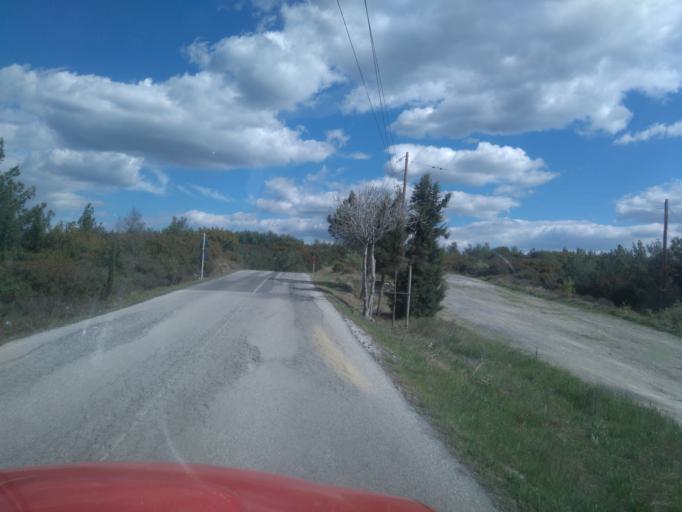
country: GR
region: Central Macedonia
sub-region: Nomos Thessalonikis
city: Pefka
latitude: 40.6436
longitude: 22.9970
